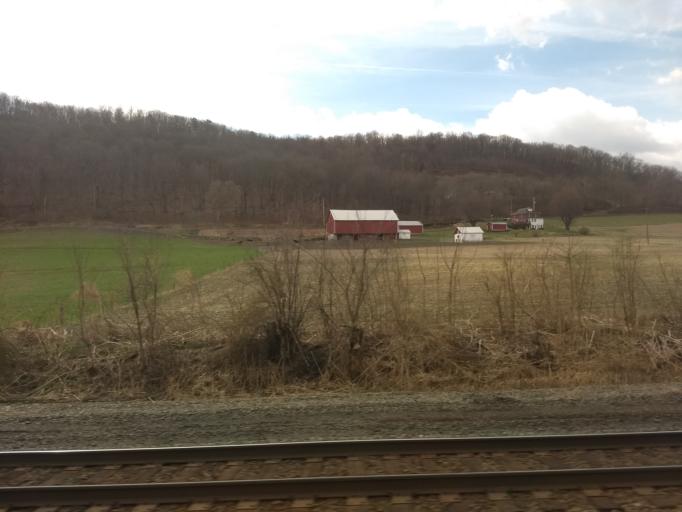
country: US
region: Pennsylvania
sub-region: Mifflin County
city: Belleville
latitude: 40.5150
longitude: -77.7022
